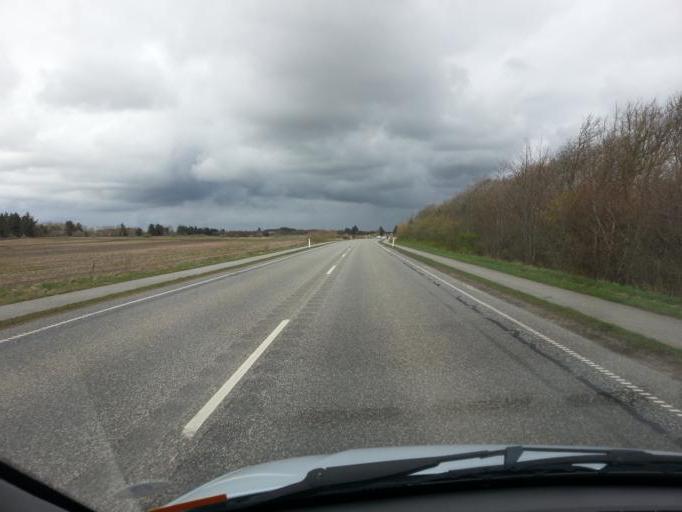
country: DK
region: Central Jutland
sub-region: Ringkobing-Skjern Kommune
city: Ringkobing
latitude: 56.1113
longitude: 8.2650
